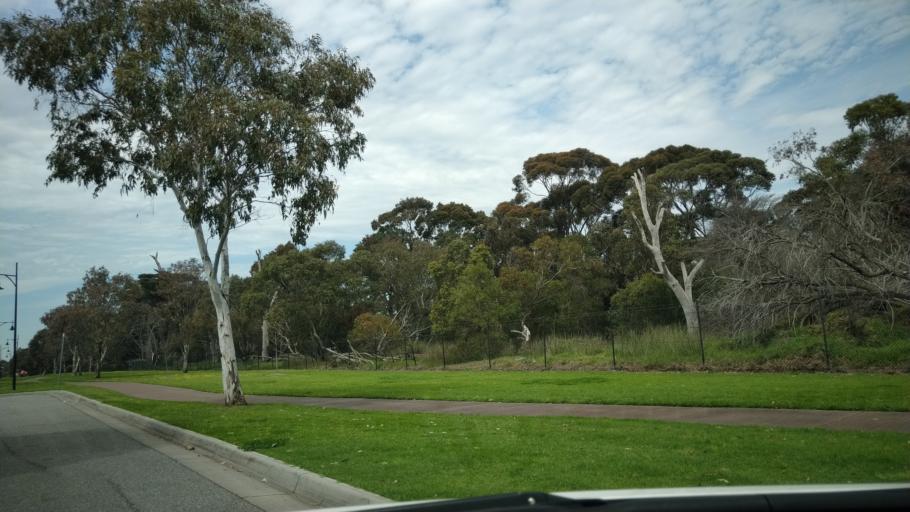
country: AU
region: Victoria
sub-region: Kingston
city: Waterways
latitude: -38.0064
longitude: 145.1515
